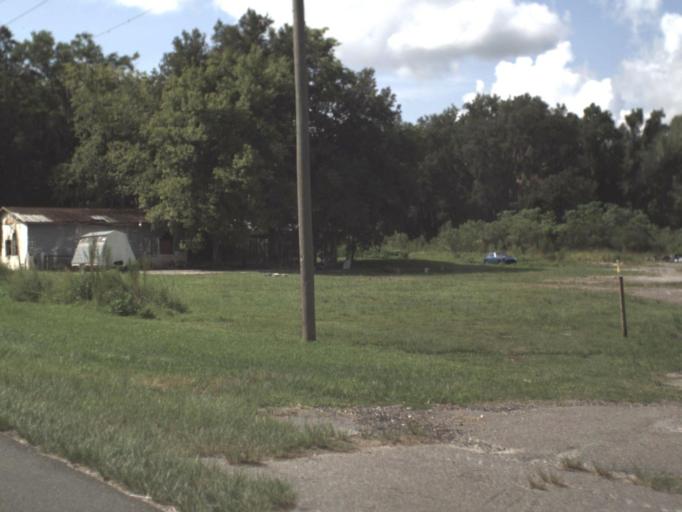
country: US
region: Florida
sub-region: Pasco County
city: Crystal Springs
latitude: 28.1969
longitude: -82.1682
